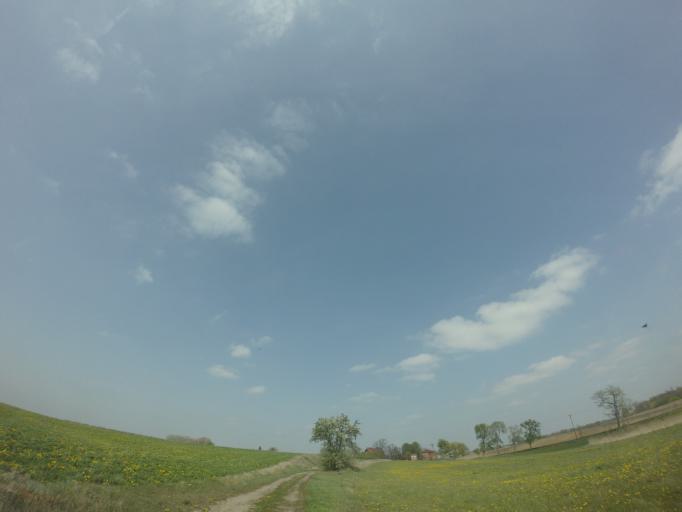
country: PL
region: West Pomeranian Voivodeship
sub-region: Powiat choszczenski
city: Pelczyce
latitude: 53.1008
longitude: 15.3334
